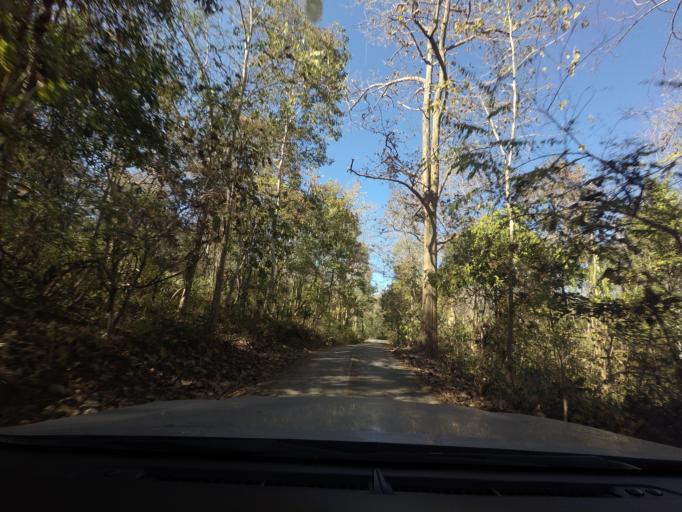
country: TH
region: Mae Hong Son
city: Wiang Nuea
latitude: 19.4008
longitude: 98.4184
